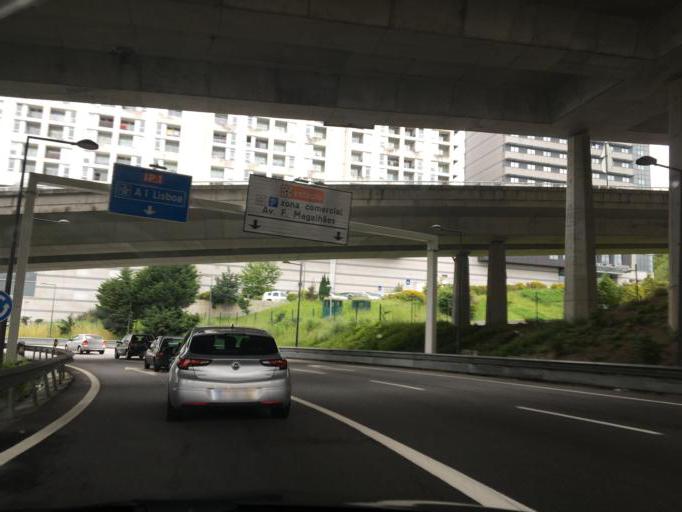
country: PT
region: Porto
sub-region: Maia
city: Pedroucos
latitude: 41.1645
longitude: -8.5818
